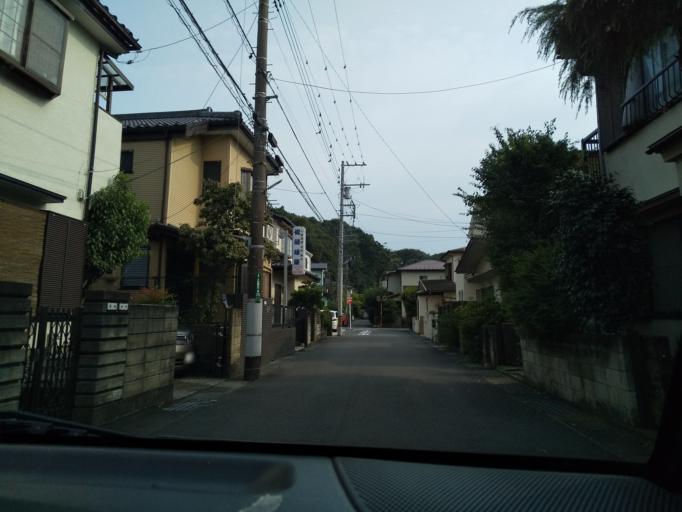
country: JP
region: Kanagawa
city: Zama
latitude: 35.4753
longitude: 139.3971
